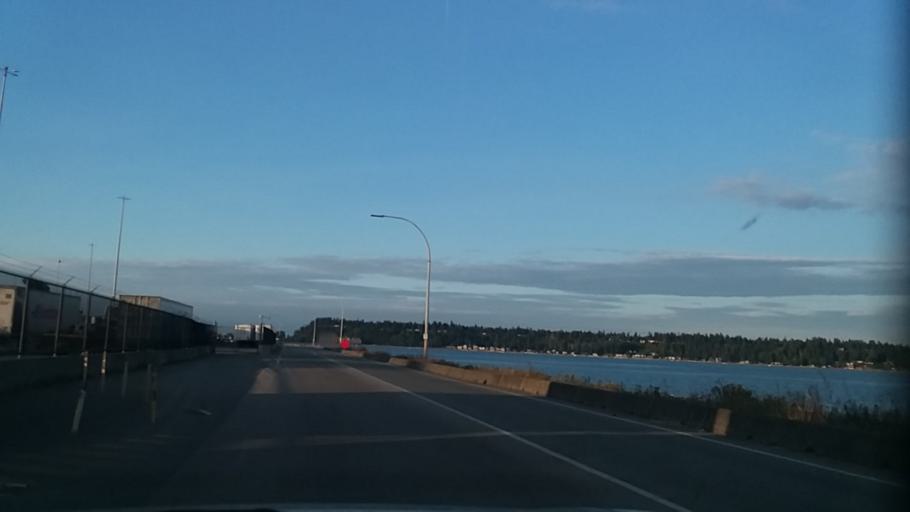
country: US
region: Washington
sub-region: Whatcom County
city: Point Roberts
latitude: 49.0082
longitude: -123.1260
